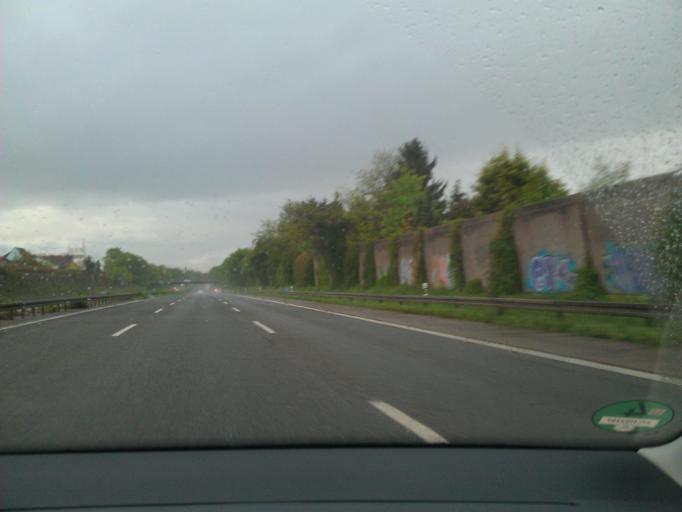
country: DE
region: North Rhine-Westphalia
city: Wesseling
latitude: 50.8151
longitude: 6.9789
